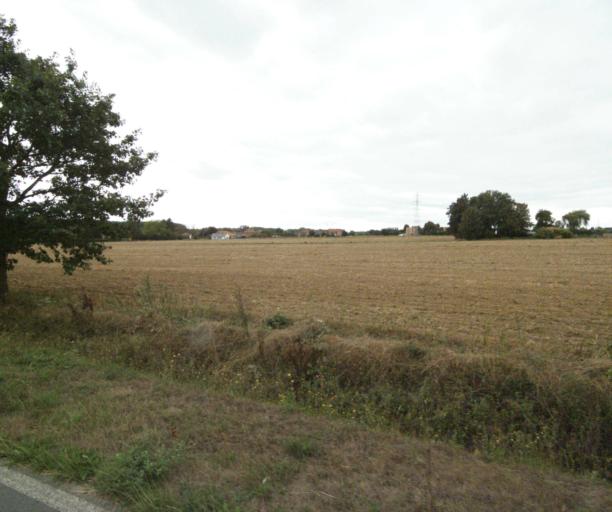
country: FR
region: Nord-Pas-de-Calais
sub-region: Departement du Nord
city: Fretin
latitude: 50.5634
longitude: 3.1606
